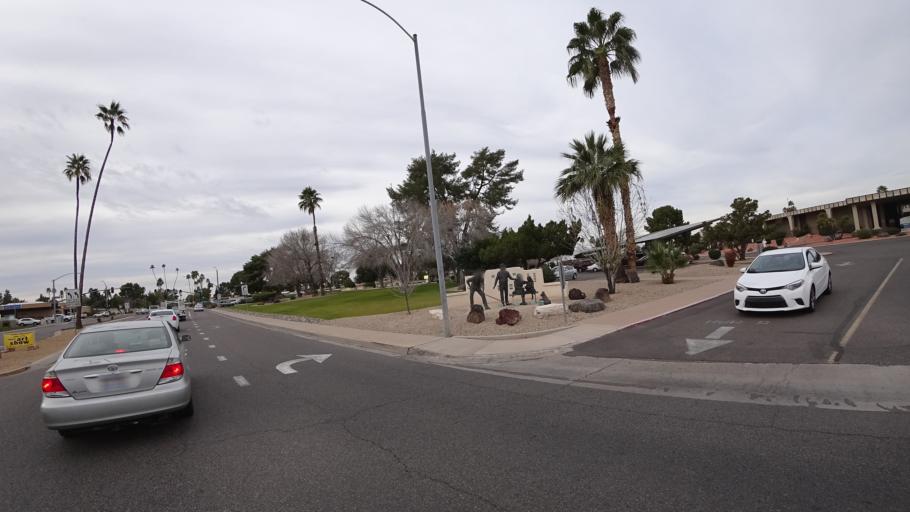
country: US
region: Arizona
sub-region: Maricopa County
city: Sun City
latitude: 33.6054
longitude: -112.2883
